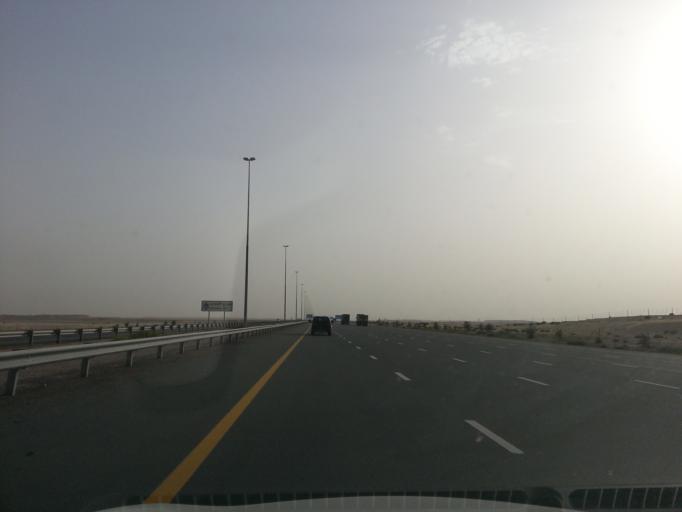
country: AE
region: Dubai
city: Dubai
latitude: 24.8244
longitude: 55.1262
